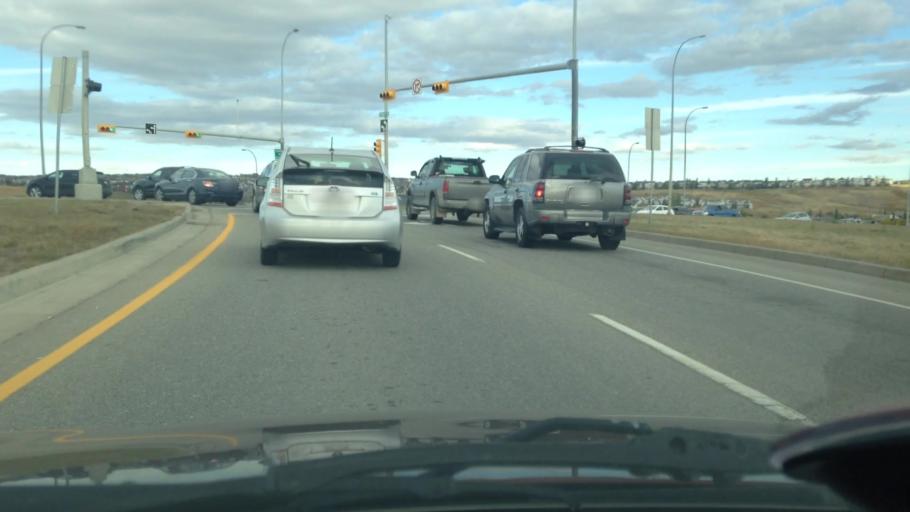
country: CA
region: Alberta
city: Calgary
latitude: 51.1561
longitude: -114.1156
